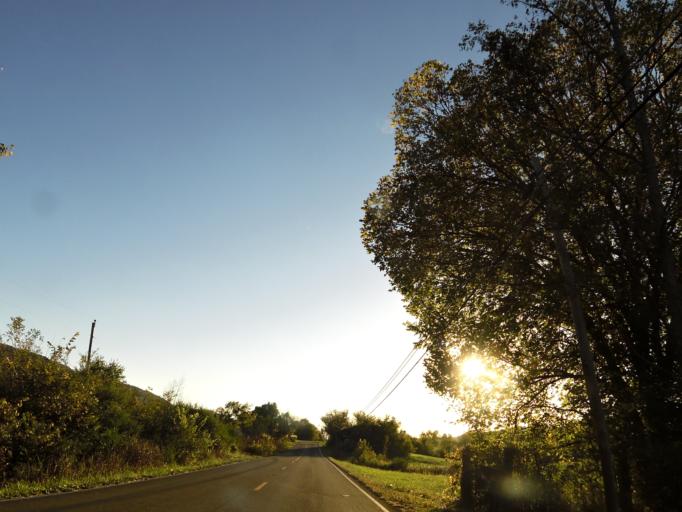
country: US
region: Tennessee
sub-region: Grainger County
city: Rutledge
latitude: 36.3025
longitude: -83.5711
